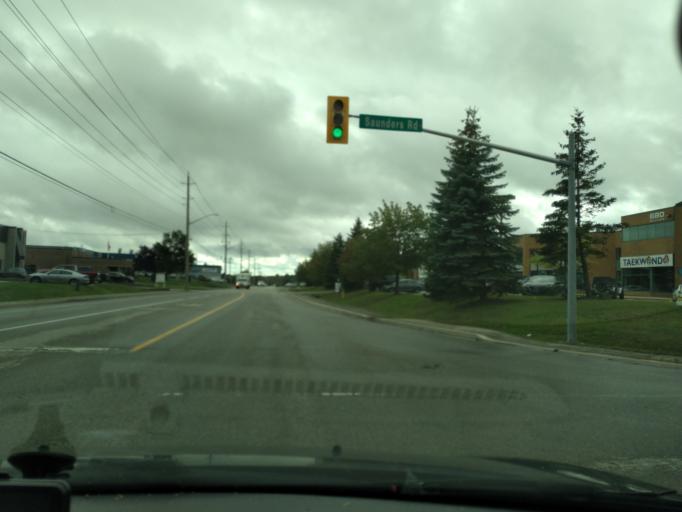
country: CA
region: Ontario
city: Innisfil
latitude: 44.3321
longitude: -79.6777
